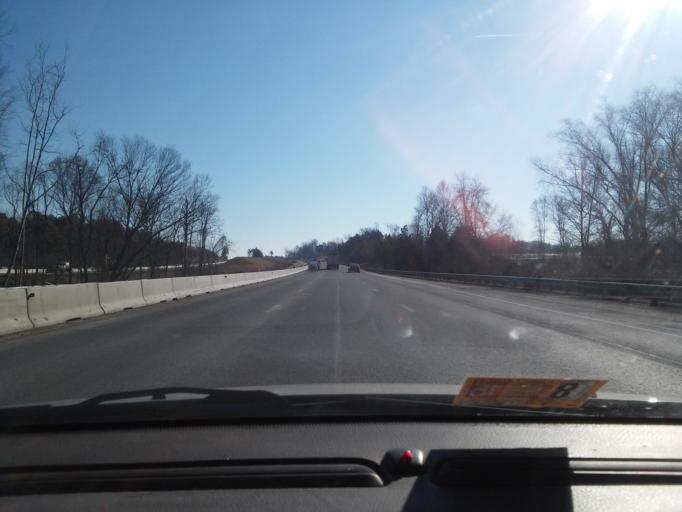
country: US
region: Virginia
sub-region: Henrico County
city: Short Pump
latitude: 37.6674
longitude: -77.6424
